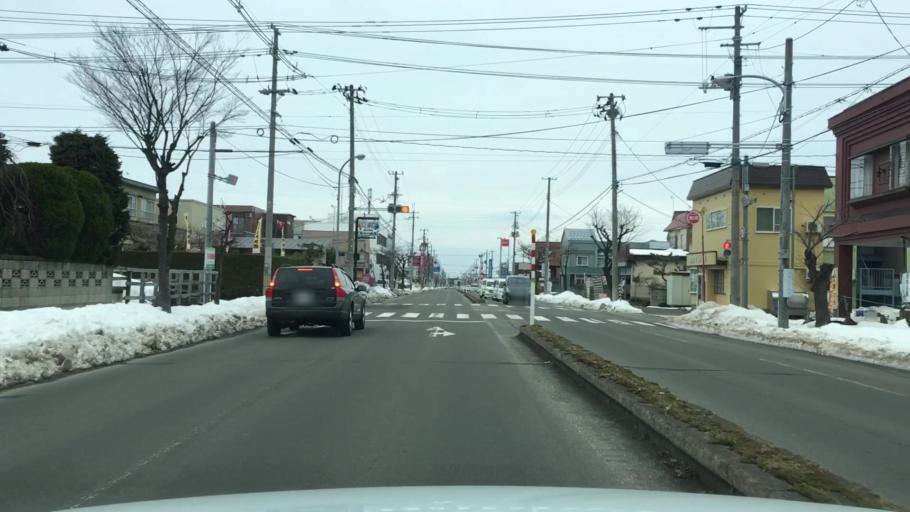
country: JP
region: Aomori
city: Hirosaki
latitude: 40.5965
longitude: 140.4924
